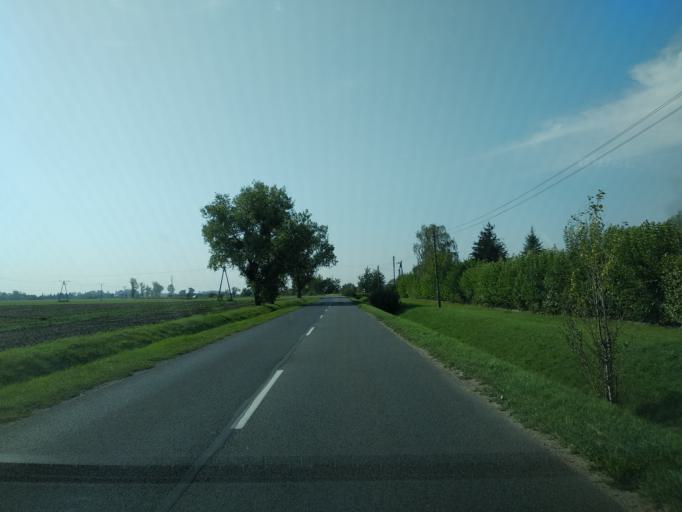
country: PL
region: Lower Silesian Voivodeship
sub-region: Powiat wroclawski
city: Zerniki Wroclawskie
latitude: 51.0454
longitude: 17.0293
